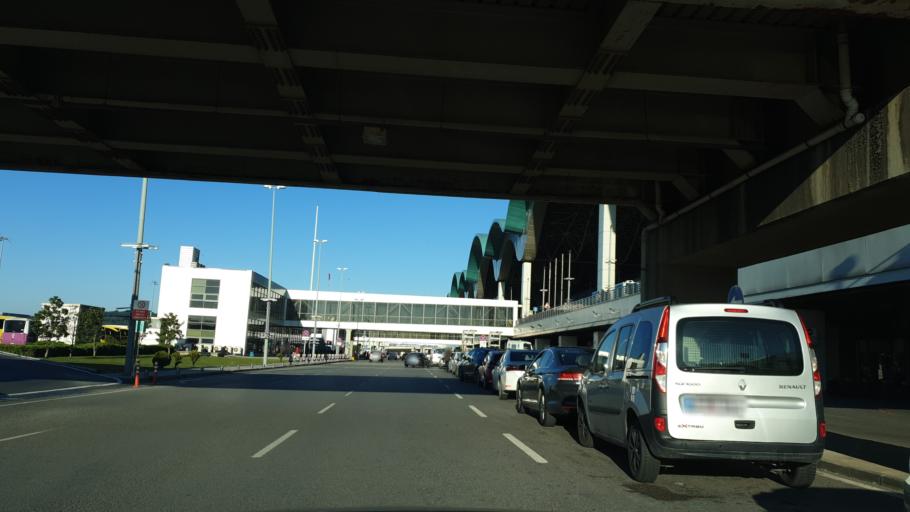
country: TR
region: Istanbul
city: Pendik
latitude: 40.9078
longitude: 29.3134
